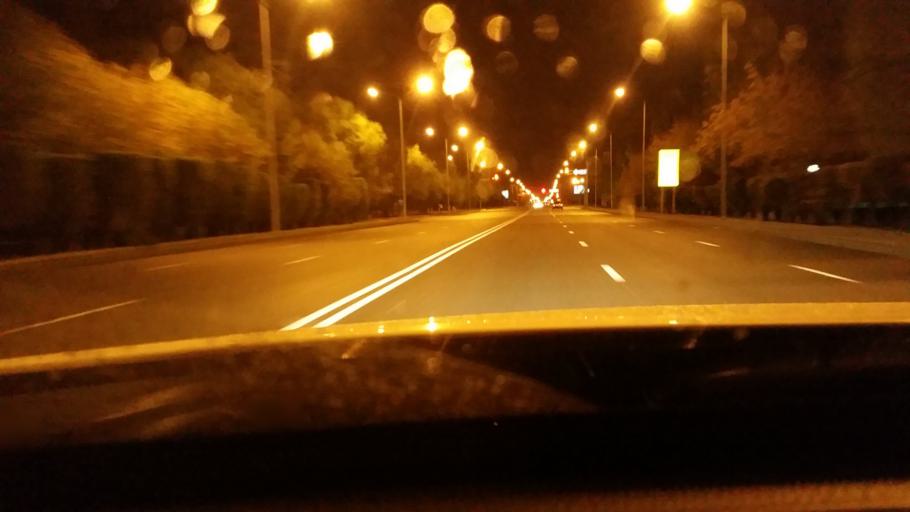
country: KZ
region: Astana Qalasy
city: Astana
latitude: 51.1531
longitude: 71.4896
